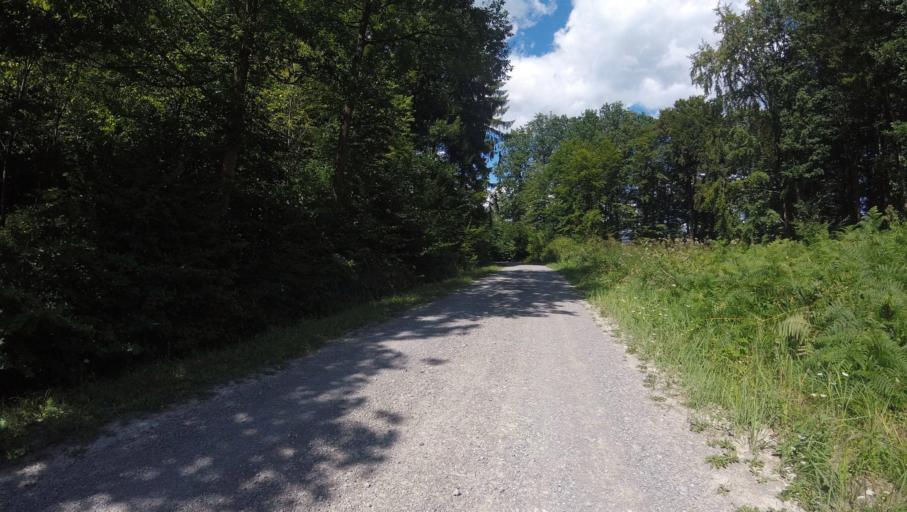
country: DE
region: Baden-Wuerttemberg
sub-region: Regierungsbezirk Stuttgart
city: Oppenweiler
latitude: 49.0093
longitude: 9.4642
